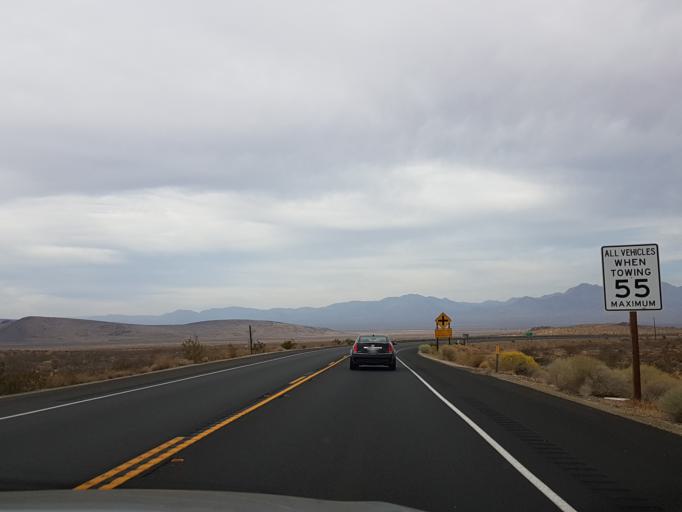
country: US
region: California
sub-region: Kern County
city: Ridgecrest
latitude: 35.5487
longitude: -117.7098
